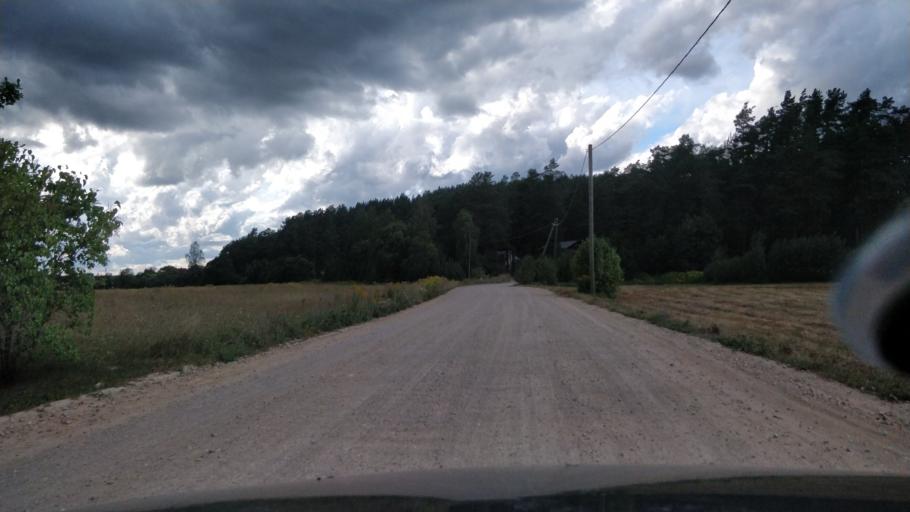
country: LV
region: Ogre
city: Ogre
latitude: 56.7947
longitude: 24.6476
